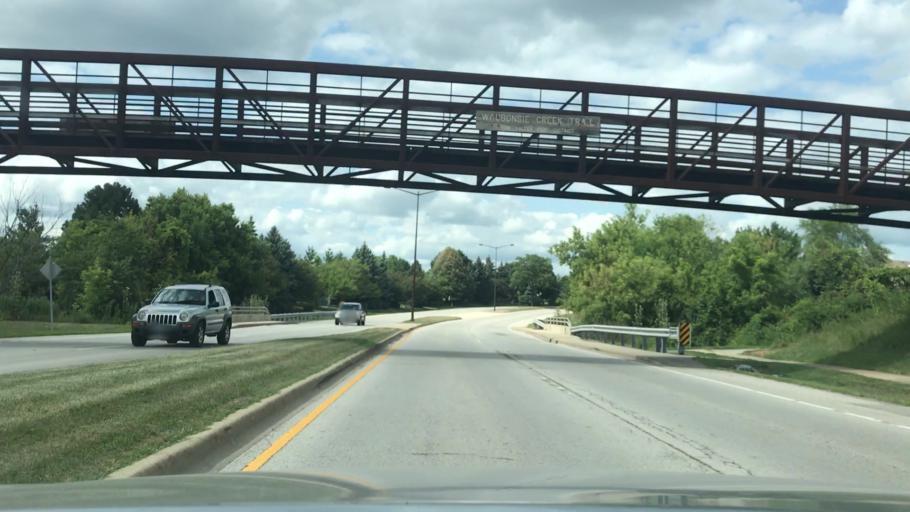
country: US
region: Illinois
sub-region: Kane County
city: Aurora
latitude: 41.7482
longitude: -88.2470
